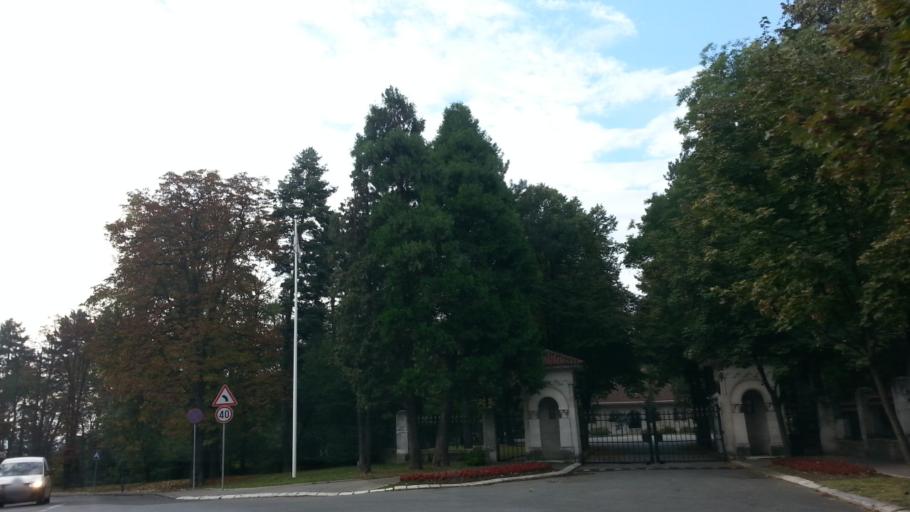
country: RS
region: Central Serbia
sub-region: Belgrade
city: Savski Venac
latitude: 44.7707
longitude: 20.4539
